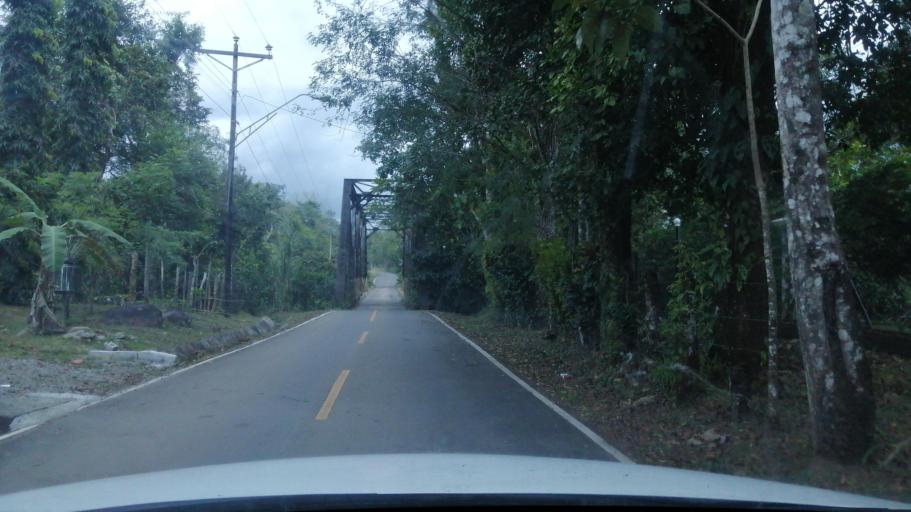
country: PA
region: Chiriqui
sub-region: Distrito Dolega
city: Pueblo Nuevo
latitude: 8.5949
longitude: -82.4140
